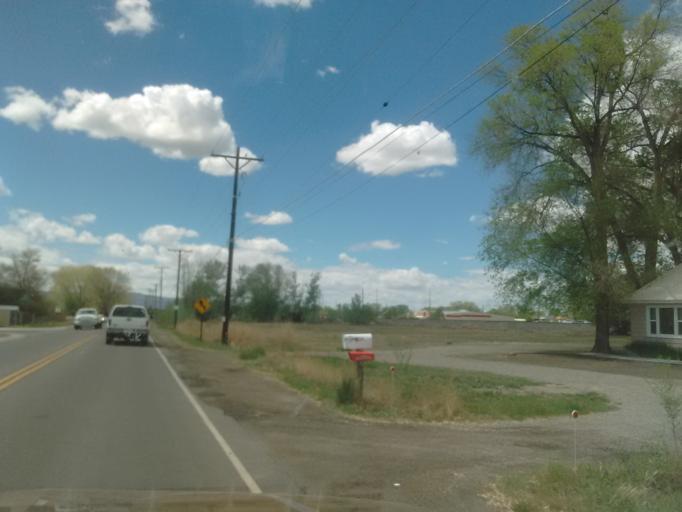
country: US
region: Colorado
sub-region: Mesa County
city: Fruitvale
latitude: 39.0773
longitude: -108.4902
